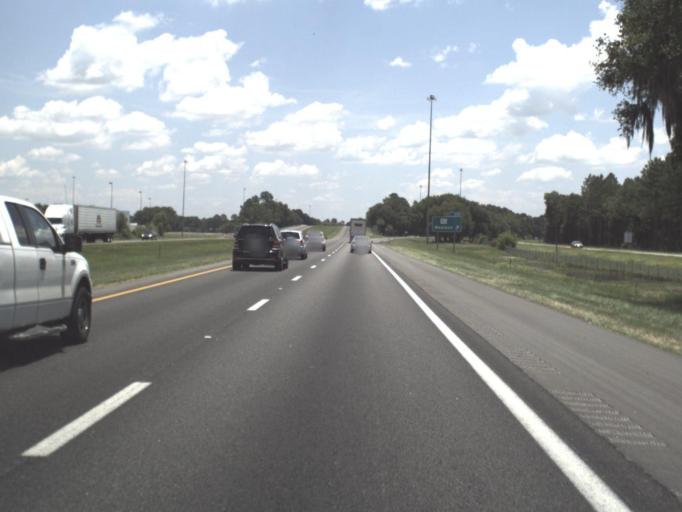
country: US
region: Florida
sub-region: Madison County
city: Madison
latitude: 30.3966
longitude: -83.3636
